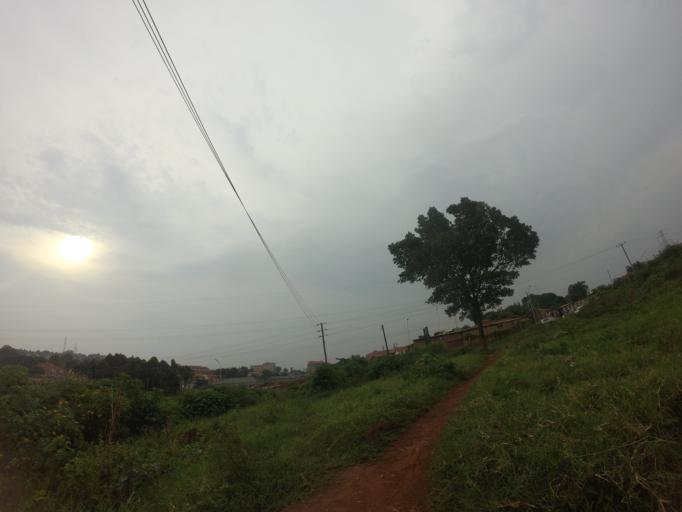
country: UG
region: Central Region
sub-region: Wakiso District
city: Kireka
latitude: 0.3570
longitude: 32.6236
